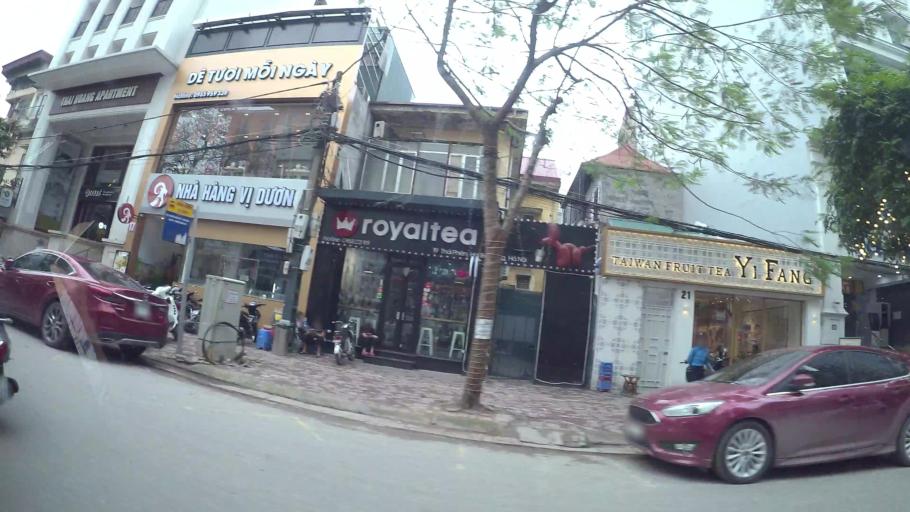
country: VN
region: Ha Noi
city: Hai BaTrung
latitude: 21.0105
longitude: 105.8503
